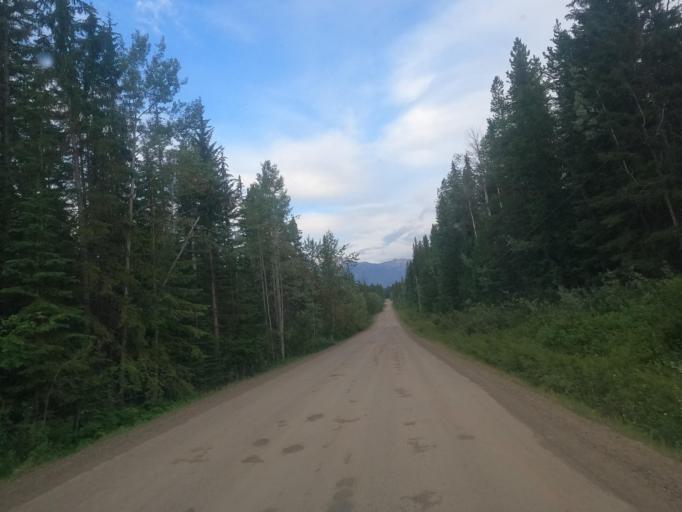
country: CA
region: British Columbia
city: Golden
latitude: 51.4384
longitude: -117.0457
